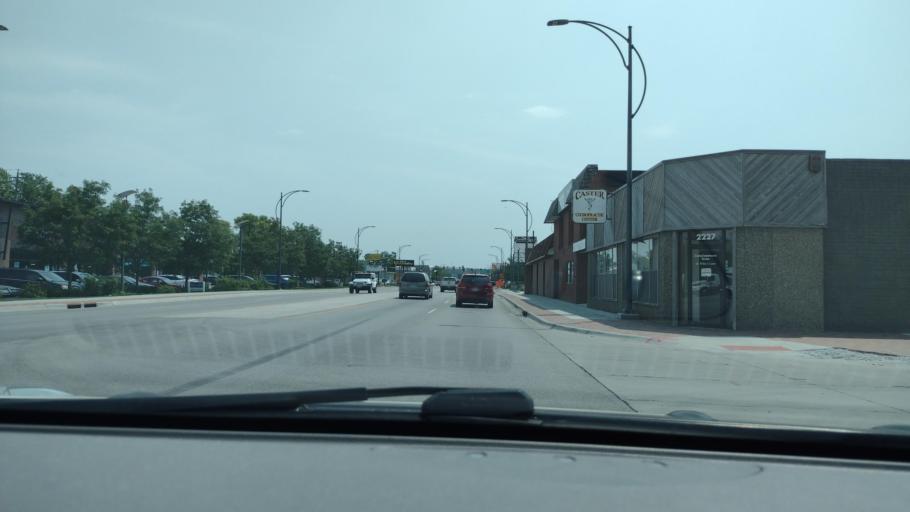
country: US
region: Iowa
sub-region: Pottawattamie County
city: Council Bluffs
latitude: 41.2619
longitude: -95.8785
